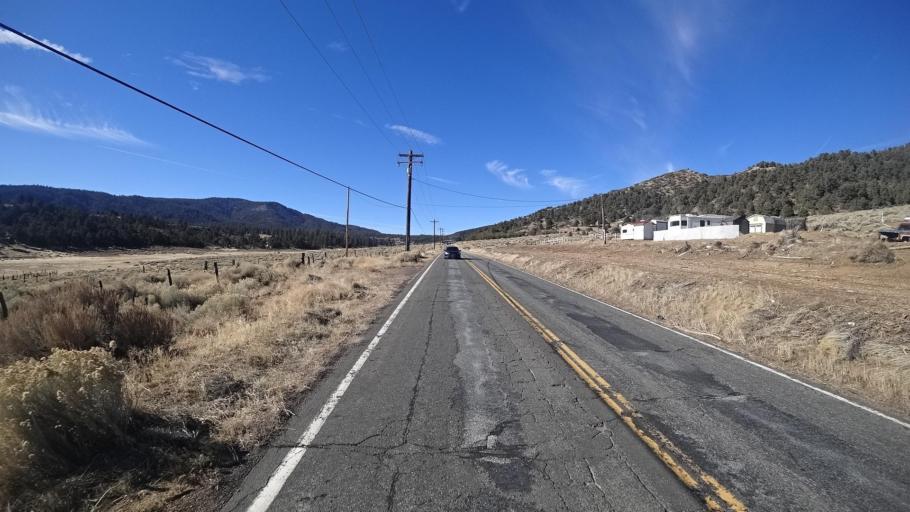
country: US
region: California
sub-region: Kern County
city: Frazier Park
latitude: 34.8377
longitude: -119.0464
